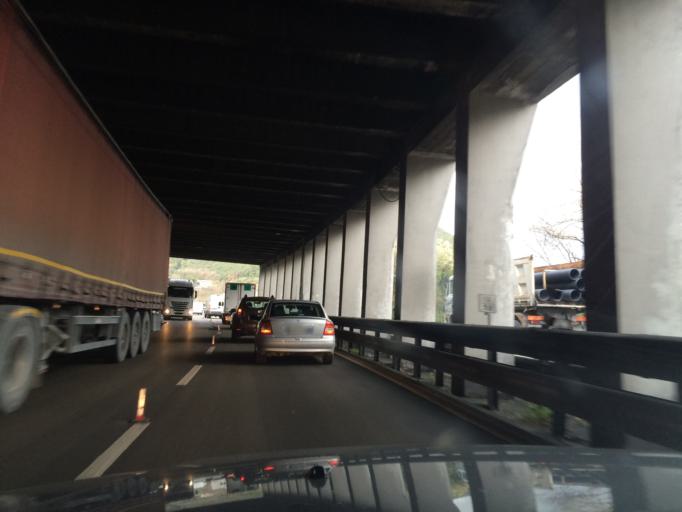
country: IT
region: Umbria
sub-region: Provincia di Terni
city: Narni Scalo
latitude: 42.5417
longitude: 12.4990
